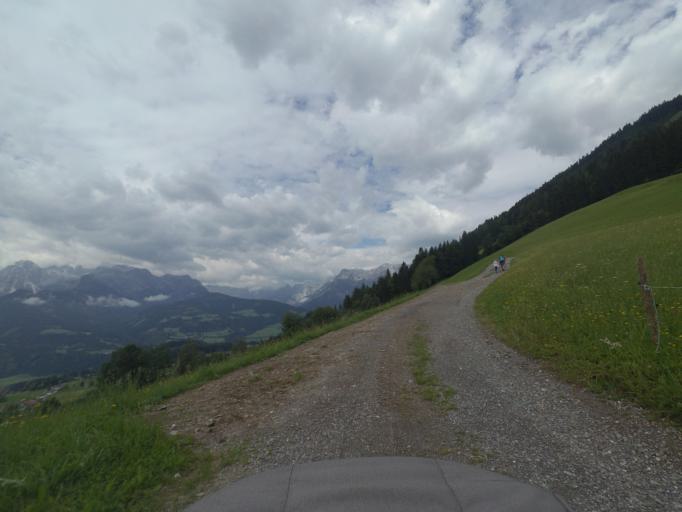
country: AT
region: Salzburg
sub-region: Politischer Bezirk Sankt Johann im Pongau
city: Werfenweng
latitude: 47.4687
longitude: 13.2375
